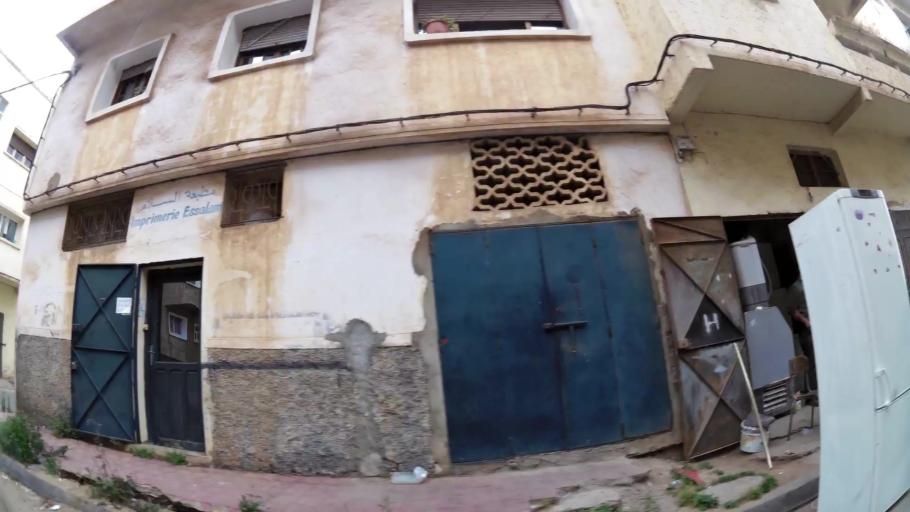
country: MA
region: Rabat-Sale-Zemmour-Zaer
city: Sale
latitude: 34.0472
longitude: -6.7935
